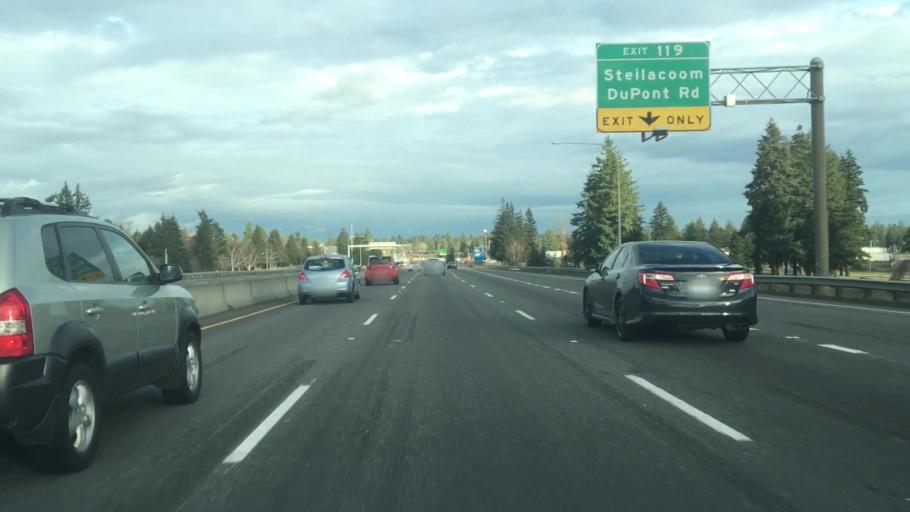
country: US
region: Washington
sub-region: Pierce County
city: DuPont
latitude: 47.0898
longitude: -122.6359
